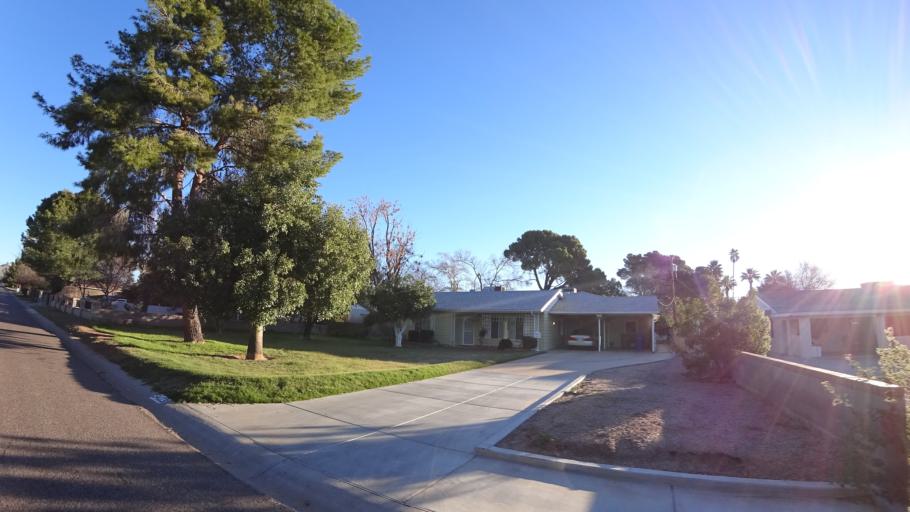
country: US
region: Arizona
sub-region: Maricopa County
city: Phoenix
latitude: 33.4887
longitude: -112.0085
